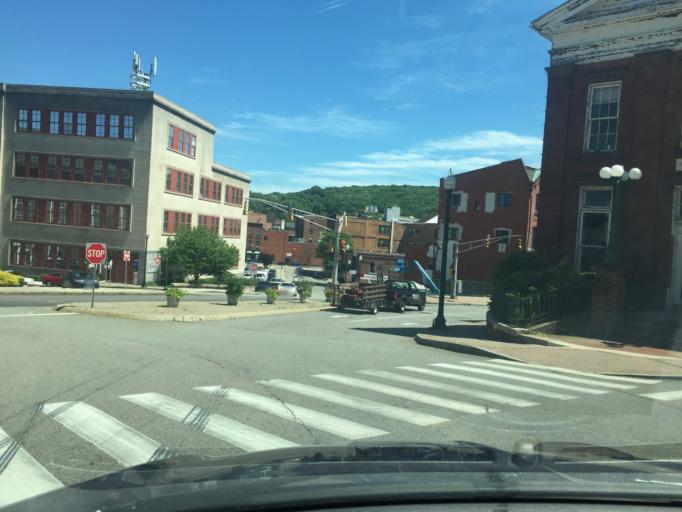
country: US
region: Connecticut
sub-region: New London County
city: Norwich
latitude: 41.5259
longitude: -72.0762
